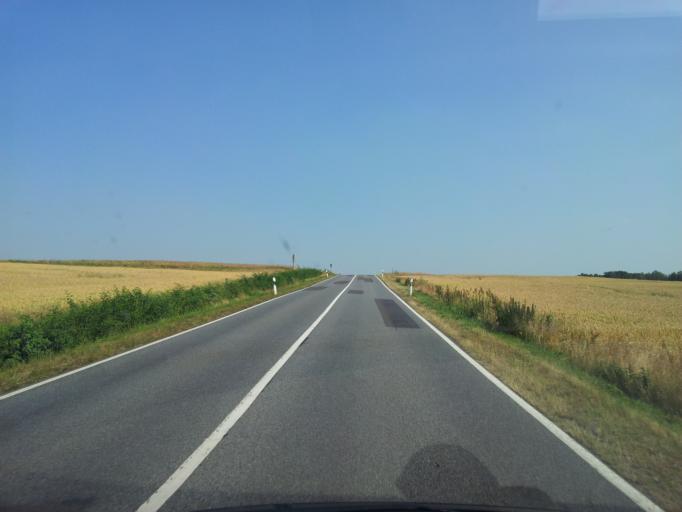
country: DE
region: Saxony
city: Wachau
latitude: 51.1518
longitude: 13.8946
